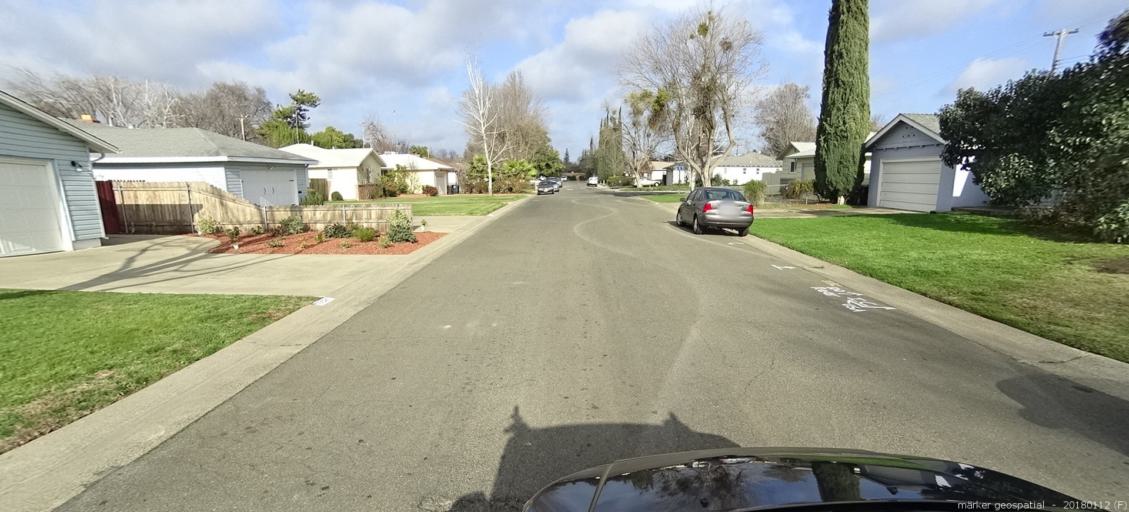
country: US
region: California
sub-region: Sacramento County
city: Rancho Cordova
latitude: 38.5988
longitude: -121.2982
